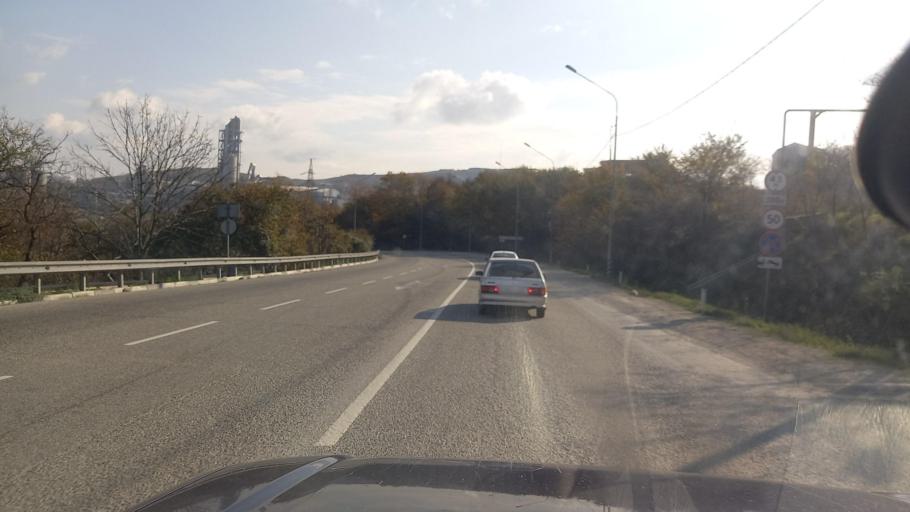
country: RU
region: Krasnodarskiy
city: Verkhnebakanskiy
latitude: 44.8365
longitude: 37.6625
